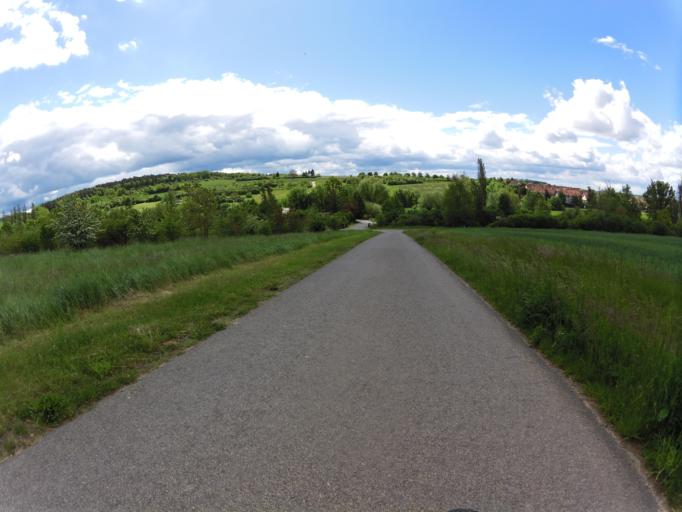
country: DE
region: Bavaria
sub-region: Regierungsbezirk Unterfranken
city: Volkach
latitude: 49.8692
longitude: 10.2420
